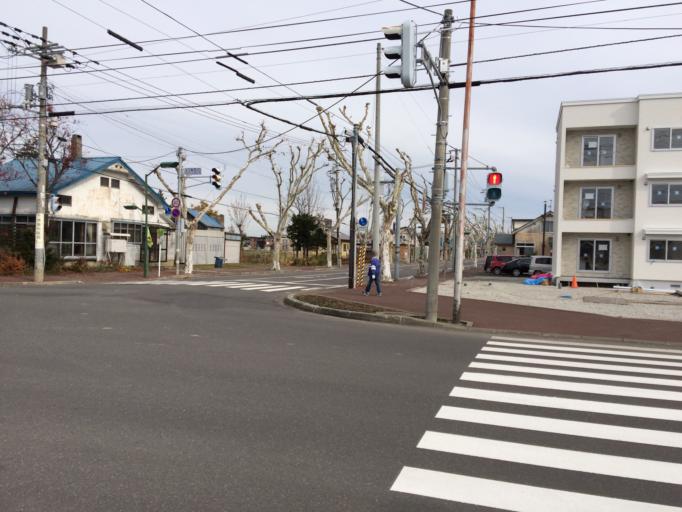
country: JP
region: Hokkaido
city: Iwamizawa
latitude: 43.2047
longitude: 141.7518
